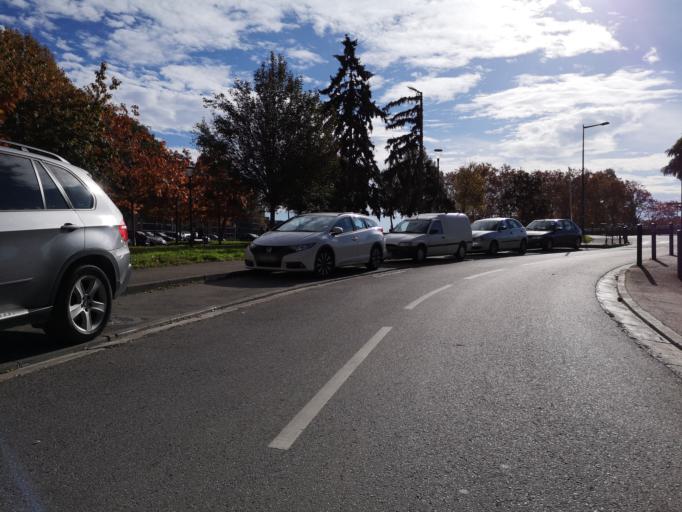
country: FR
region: Midi-Pyrenees
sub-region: Departement de la Haute-Garonne
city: Toulouse
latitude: 43.5949
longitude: 1.4412
